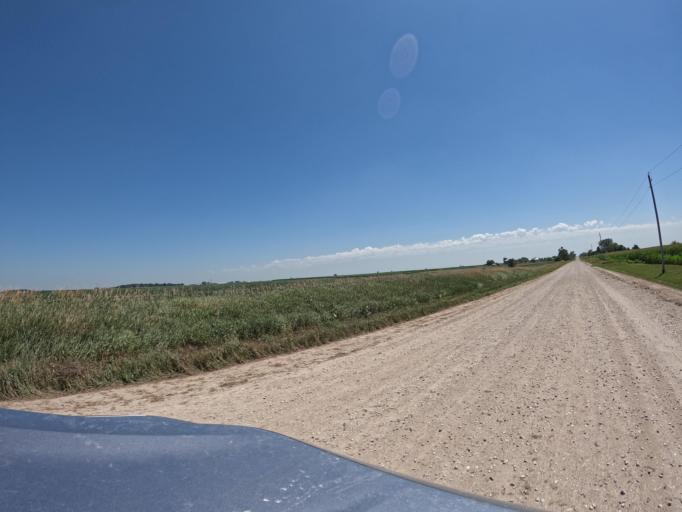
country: US
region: Iowa
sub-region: Poweshiek County
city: Montezuma
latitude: 41.4762
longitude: -92.3935
